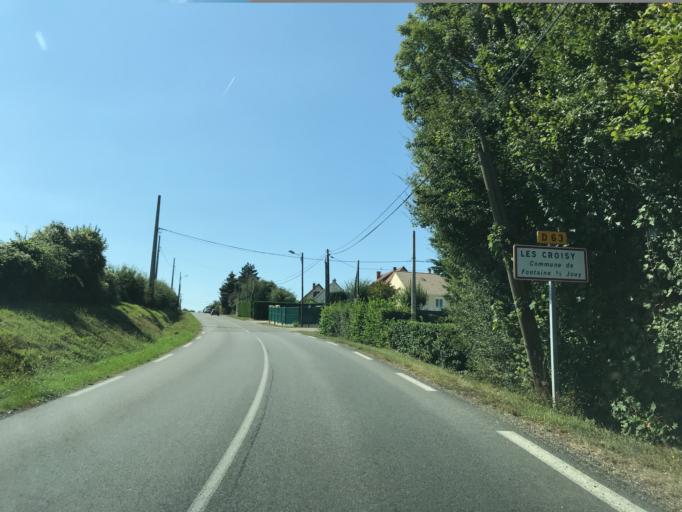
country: FR
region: Haute-Normandie
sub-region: Departement de l'Eure
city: Houlbec-Cocherel
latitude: 49.0617
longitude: 1.2739
